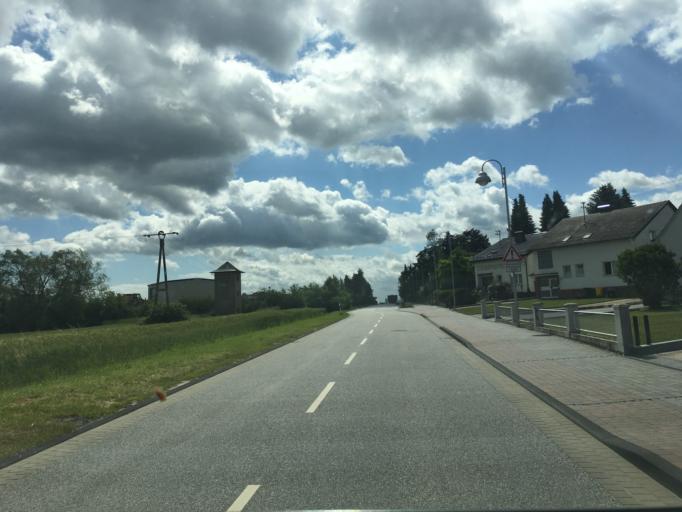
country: DE
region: Rheinland-Pfalz
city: Bad Neuenahr-Ahrweiler
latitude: 50.5703
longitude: 7.0996
